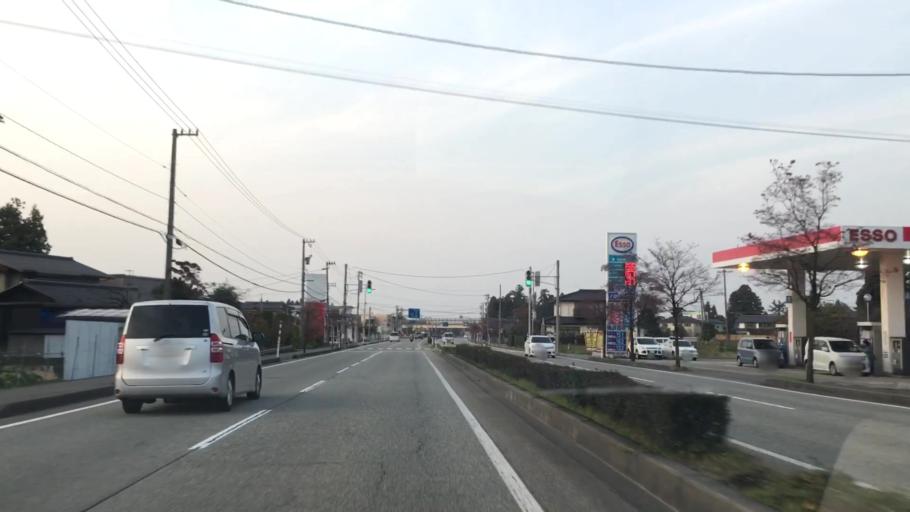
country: JP
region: Toyama
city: Toyama-shi
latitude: 36.6426
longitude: 137.2362
